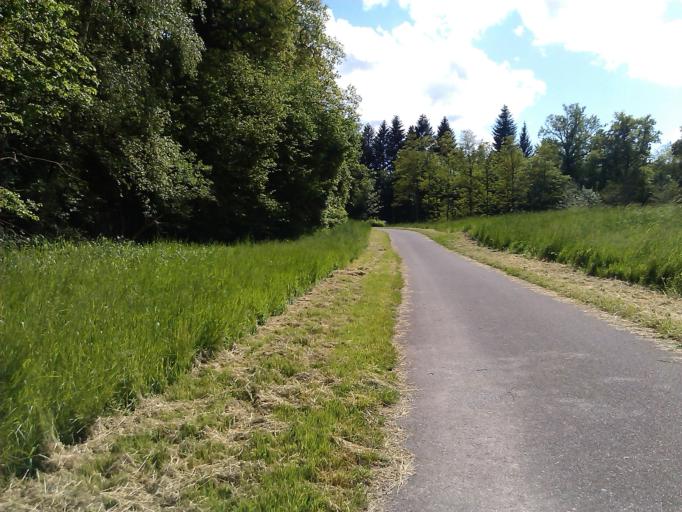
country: FR
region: Bourgogne
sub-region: Departement de Saone-et-Loire
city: Ecuisses
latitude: 46.7776
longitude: 4.5445
